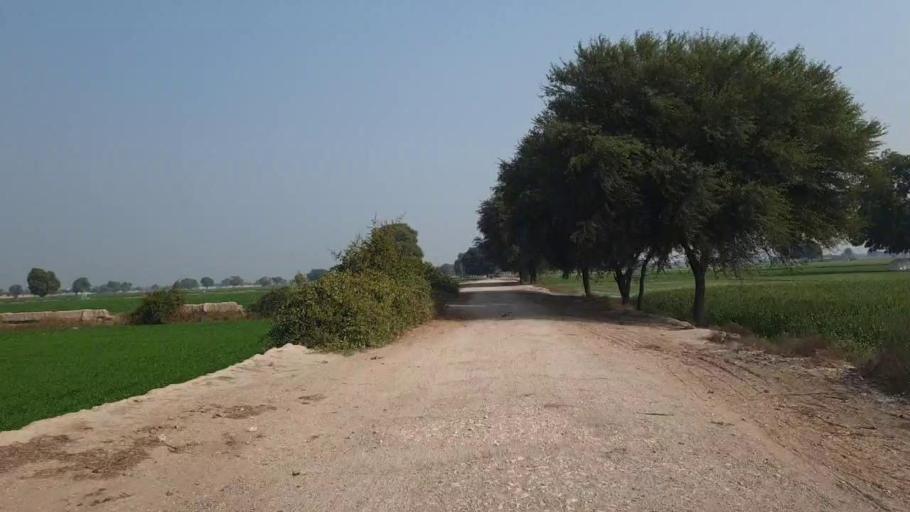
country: PK
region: Sindh
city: Hala
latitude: 25.8289
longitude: 68.4564
